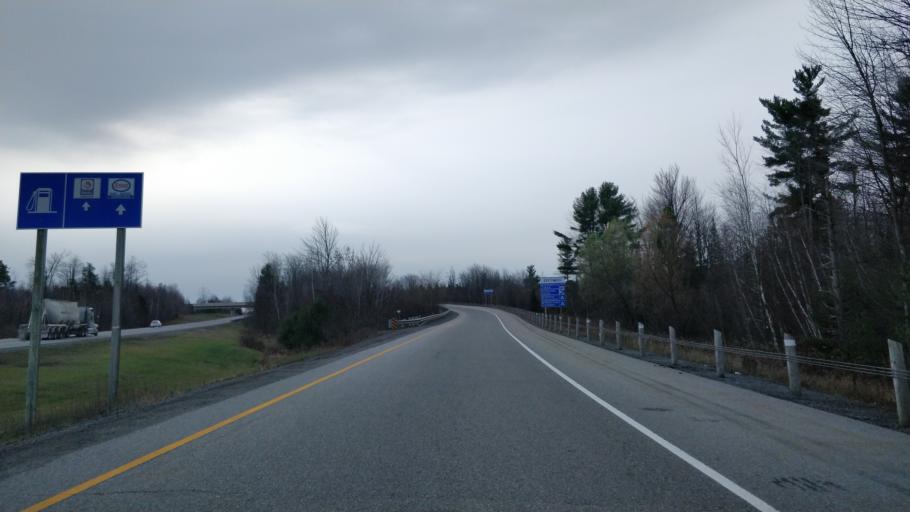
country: CA
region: Ontario
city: Prescott
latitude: 44.7650
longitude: -75.4988
